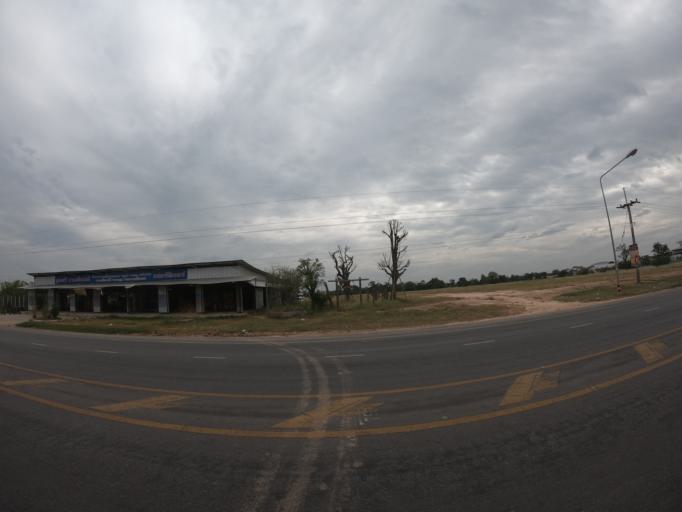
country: TH
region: Roi Et
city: Thawat Buri
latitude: 16.0821
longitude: 103.7088
